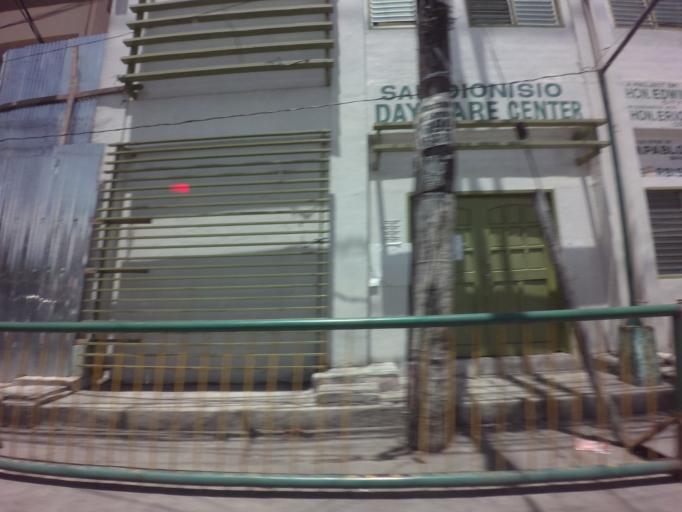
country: PH
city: Sambayanihan People's Village
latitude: 14.4910
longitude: 120.9892
